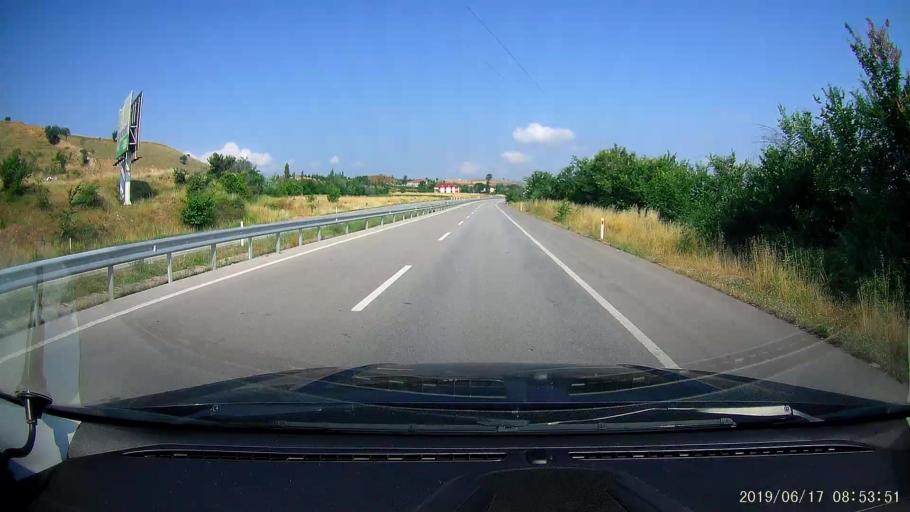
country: TR
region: Amasya
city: Esencay
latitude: 40.7134
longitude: 36.4728
